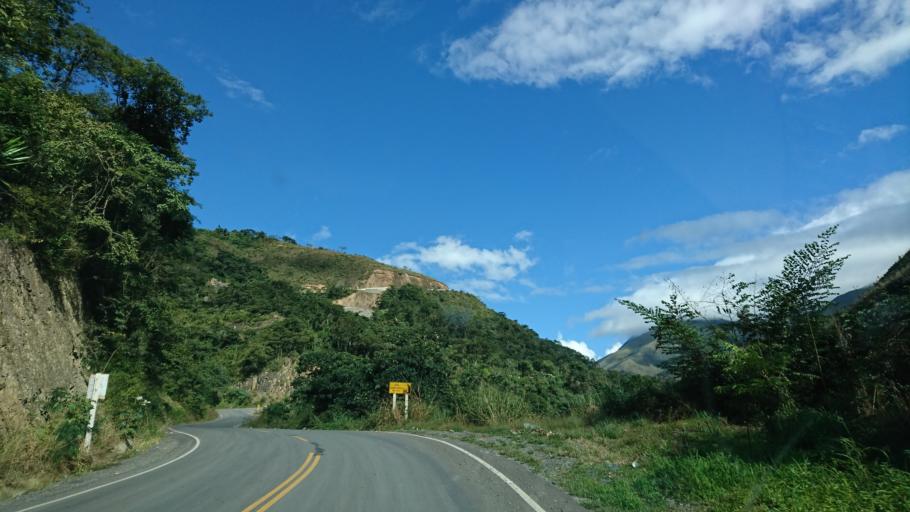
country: BO
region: La Paz
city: Coroico
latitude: -16.1960
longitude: -67.7427
